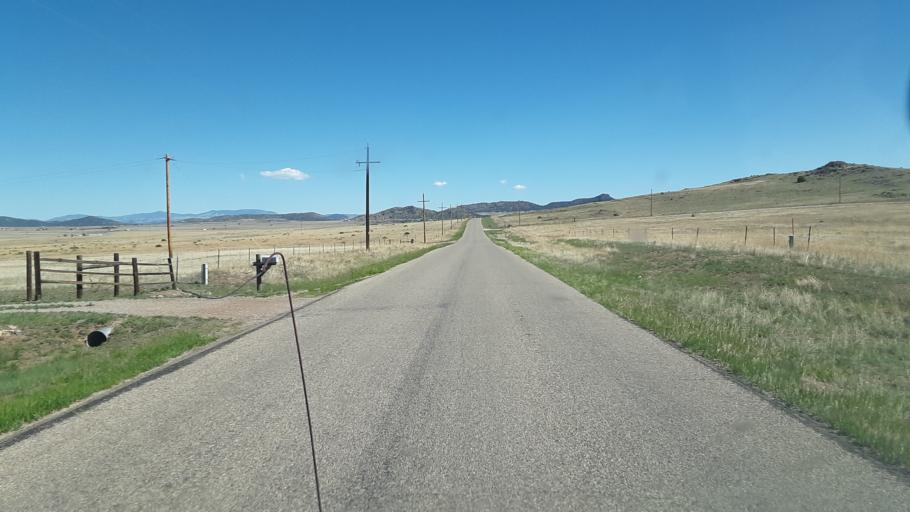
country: US
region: Colorado
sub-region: Custer County
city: Westcliffe
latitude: 38.1749
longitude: -105.4617
